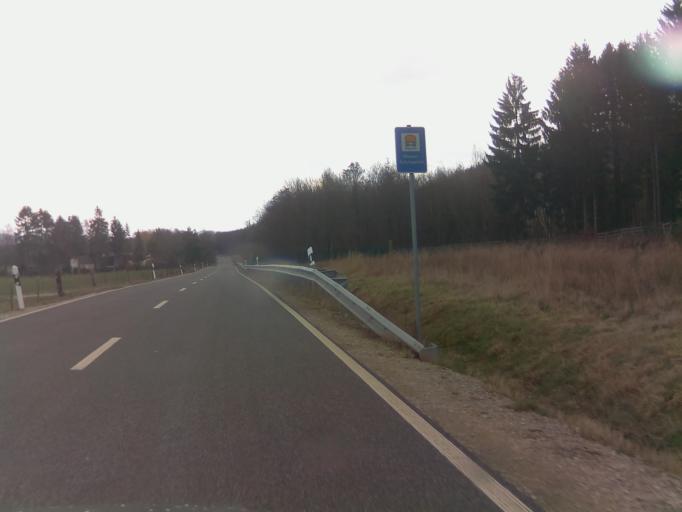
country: DE
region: Rheinland-Pfalz
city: Dorrebach
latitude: 49.9542
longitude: 7.6649
